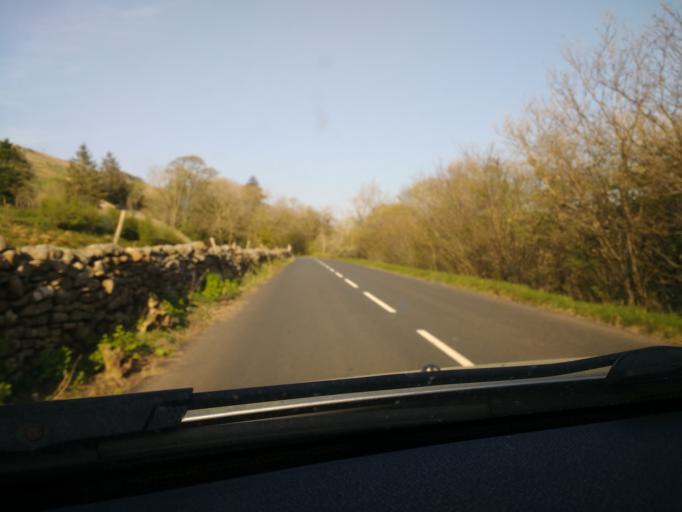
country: GB
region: England
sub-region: Cumbria
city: Sedbergh
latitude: 54.3007
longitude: -2.3980
